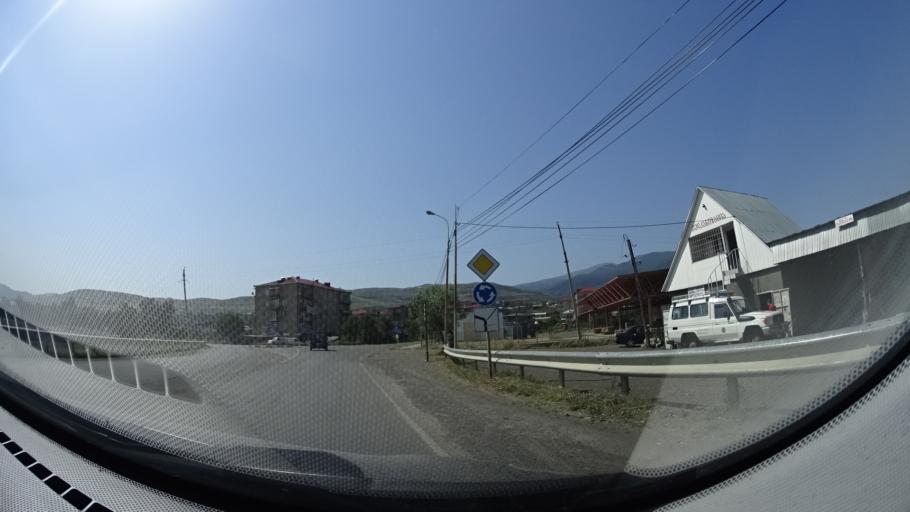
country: GE
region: Samtskhe-Javakheti
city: Akhaltsikhe
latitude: 41.6451
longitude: 43.0021
